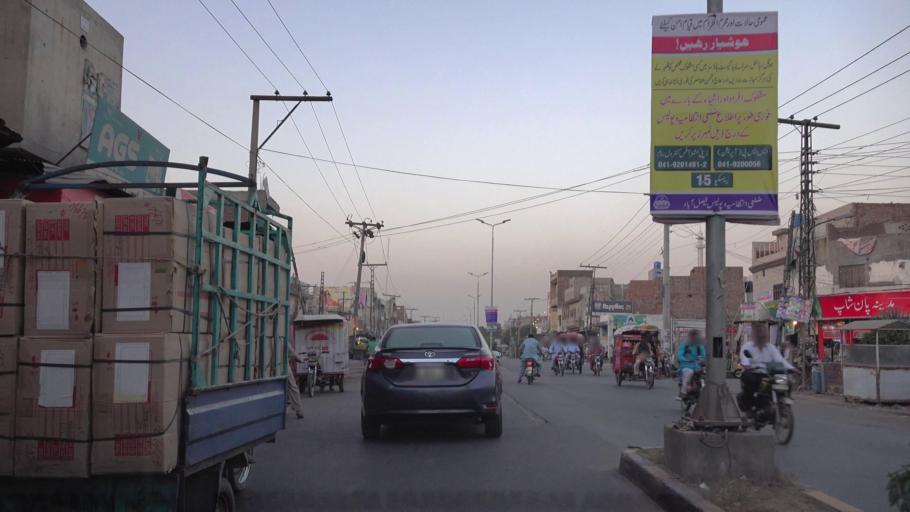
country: PK
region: Punjab
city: Faisalabad
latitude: 31.4468
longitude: 73.0965
